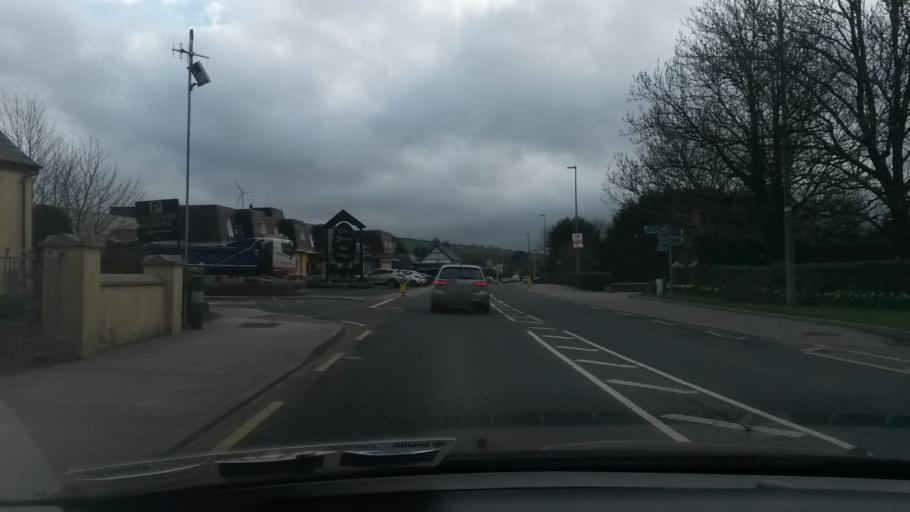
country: IE
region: Munster
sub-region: County Limerick
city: Newcastle West
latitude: 52.3980
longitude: -9.1736
